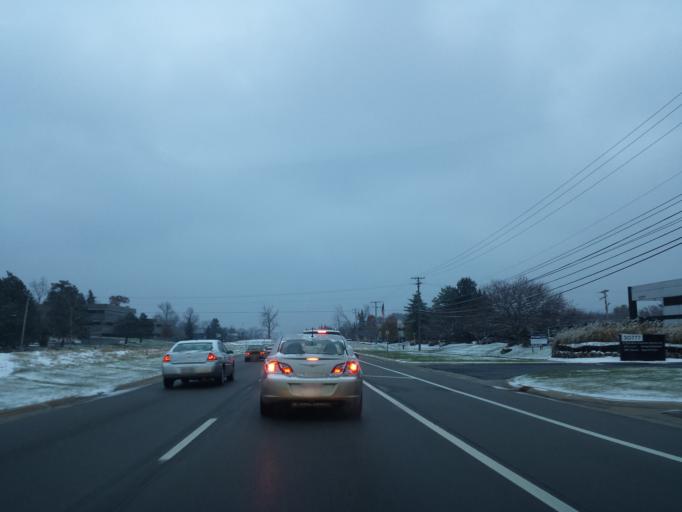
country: US
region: Michigan
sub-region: Oakland County
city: Franklin
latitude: 42.5128
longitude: -83.3302
